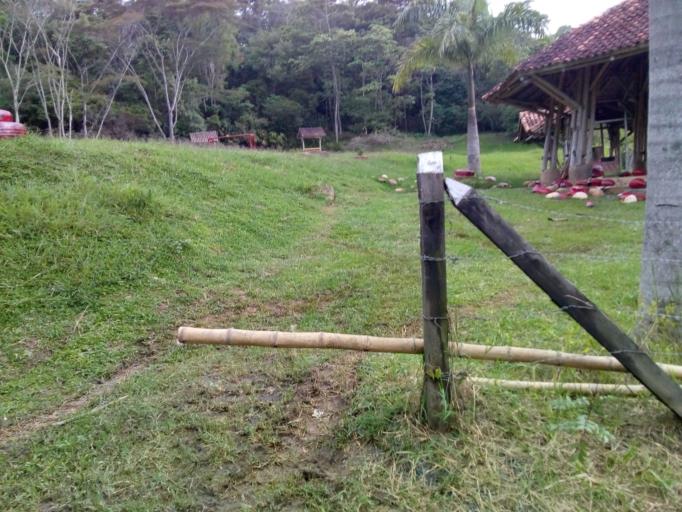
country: CO
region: Santander
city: Guepsa
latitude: 6.0214
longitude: -73.5476
